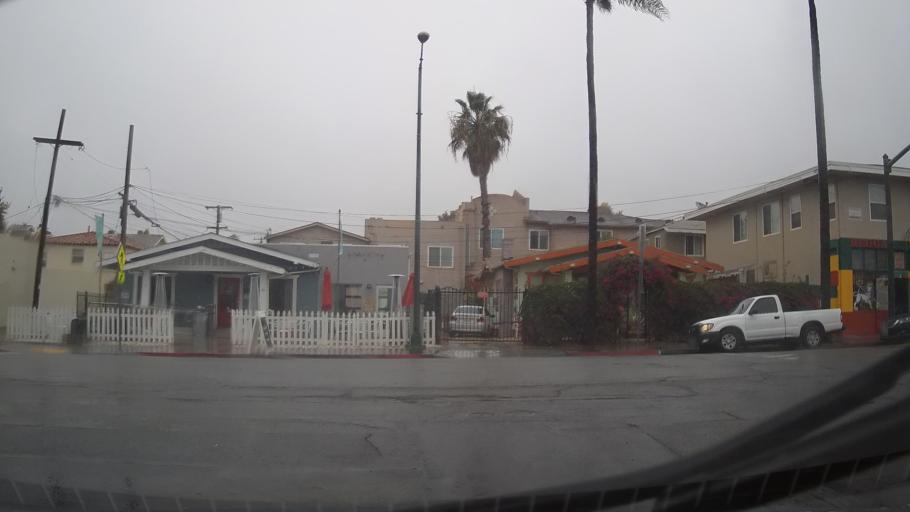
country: US
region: California
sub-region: San Diego County
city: San Diego
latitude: 32.7483
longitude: -117.1368
